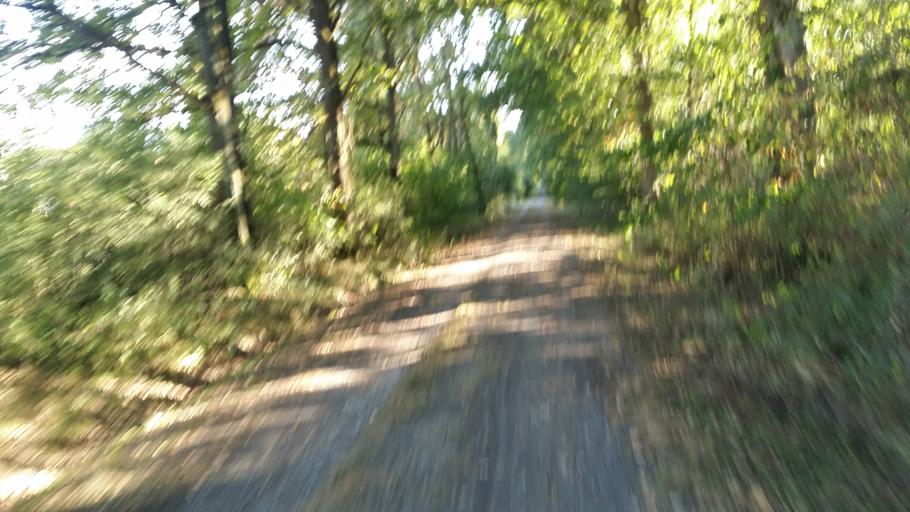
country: DE
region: Hesse
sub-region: Regierungsbezirk Giessen
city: Giessen
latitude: 50.5781
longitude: 8.7244
